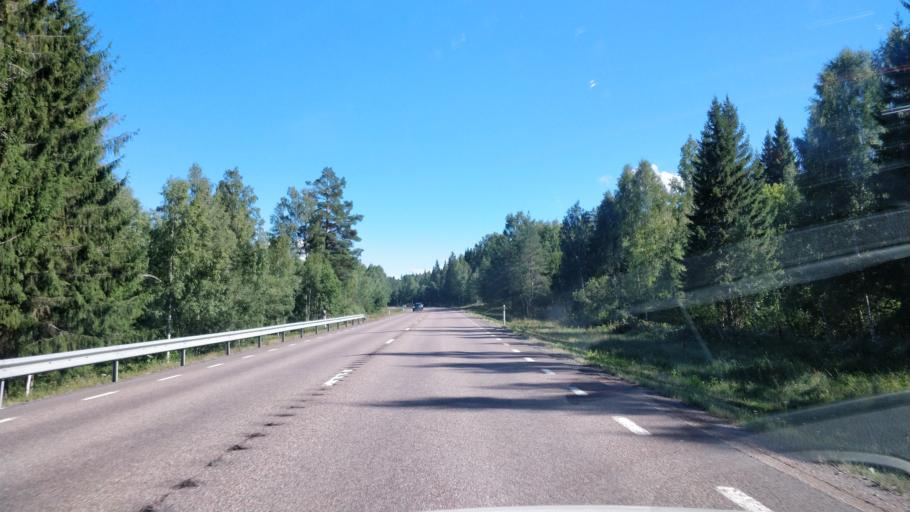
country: SE
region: Dalarna
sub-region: Faluns Kommun
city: Falun
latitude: 60.6447
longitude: 15.5720
